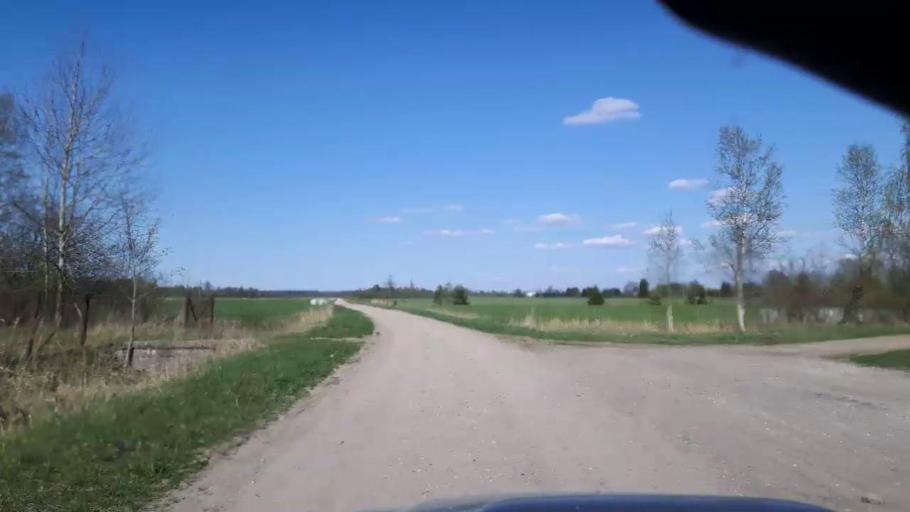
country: EE
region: Paernumaa
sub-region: Tootsi vald
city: Tootsi
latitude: 58.5259
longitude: 24.8226
